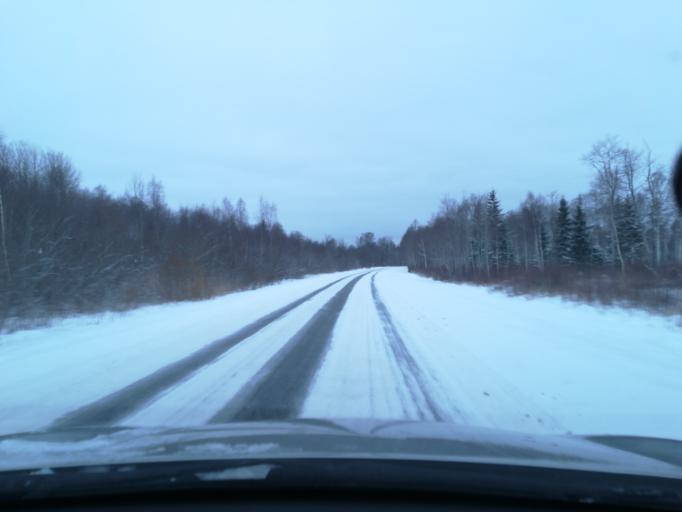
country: EE
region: Harju
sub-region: Keila linn
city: Keila
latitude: 59.3805
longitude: 24.3021
